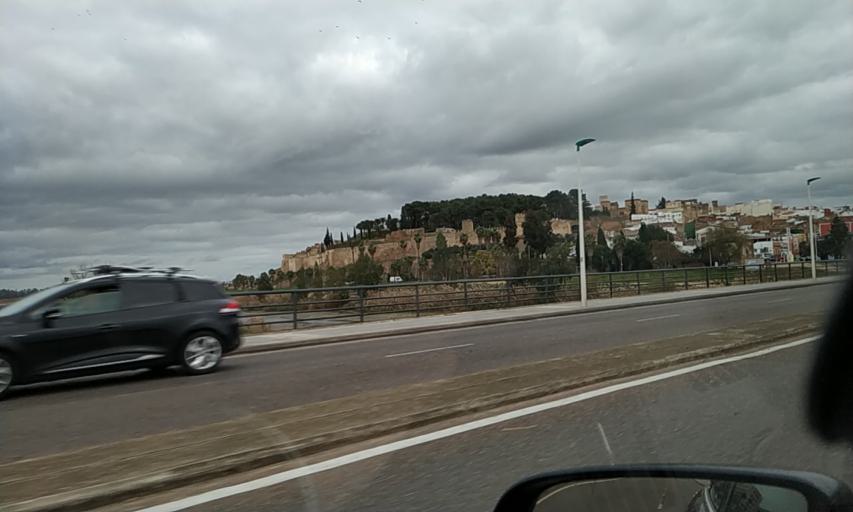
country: ES
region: Extremadura
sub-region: Provincia de Badajoz
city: Badajoz
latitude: 38.8845
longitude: -6.9741
